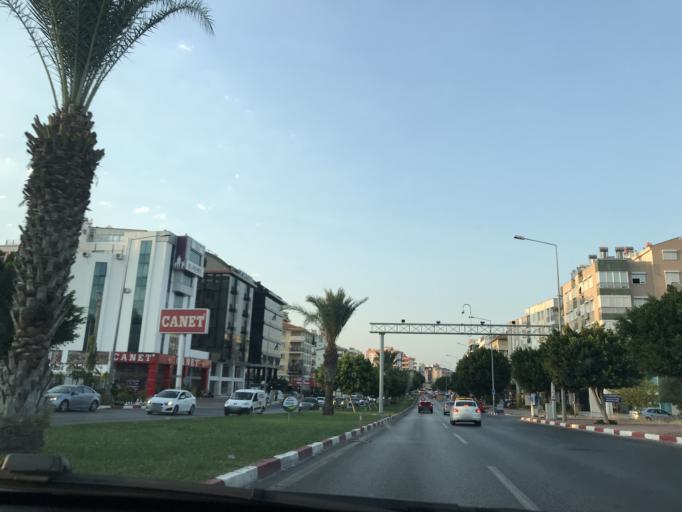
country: TR
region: Antalya
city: Antalya
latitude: 36.8718
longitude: 30.6415
